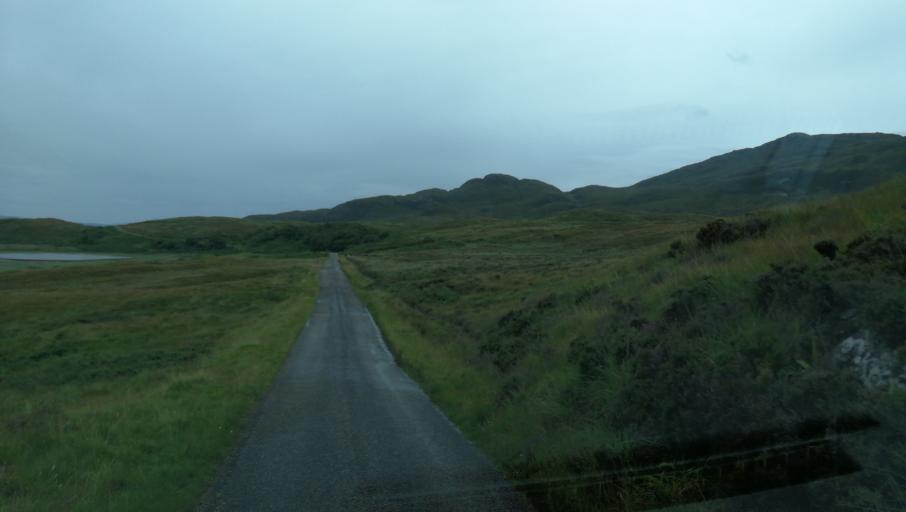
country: GB
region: Scotland
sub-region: Argyll and Bute
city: Isle Of Mull
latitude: 56.7163
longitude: -6.1495
